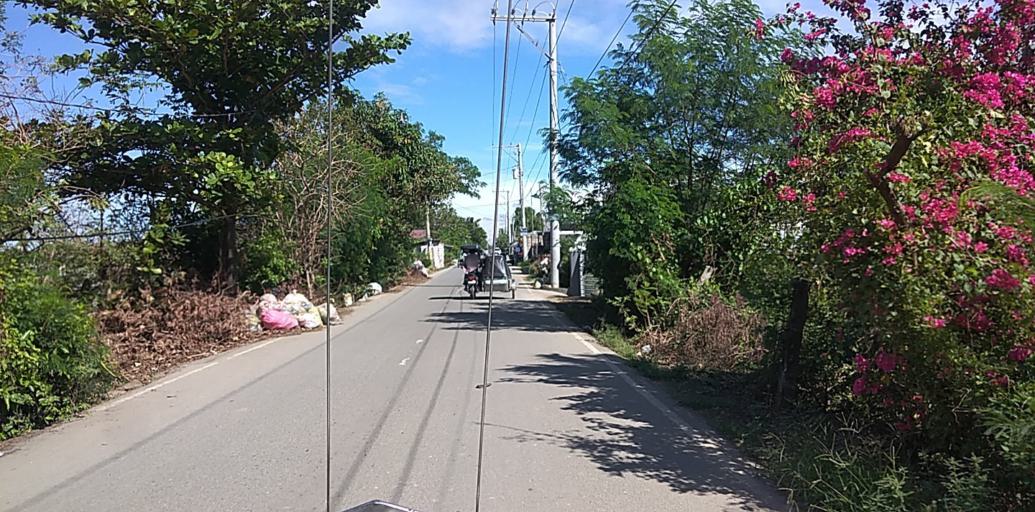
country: PH
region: Central Luzon
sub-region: Province of Pampanga
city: Candaba
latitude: 15.0867
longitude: 120.8105
